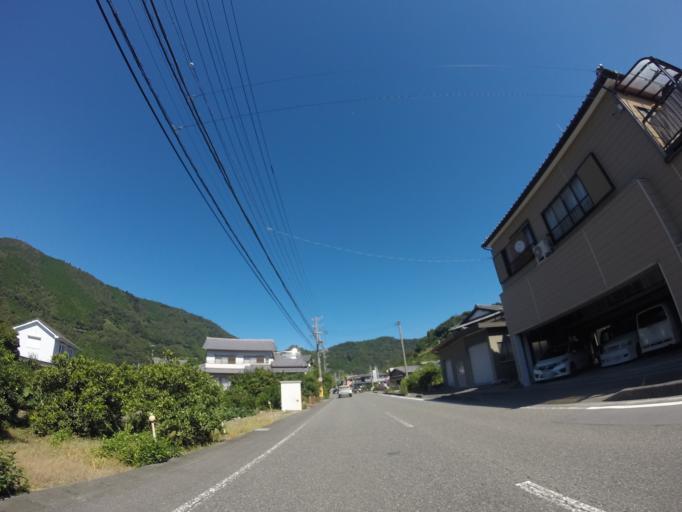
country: JP
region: Shizuoka
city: Kanaya
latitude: 34.8774
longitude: 138.1062
